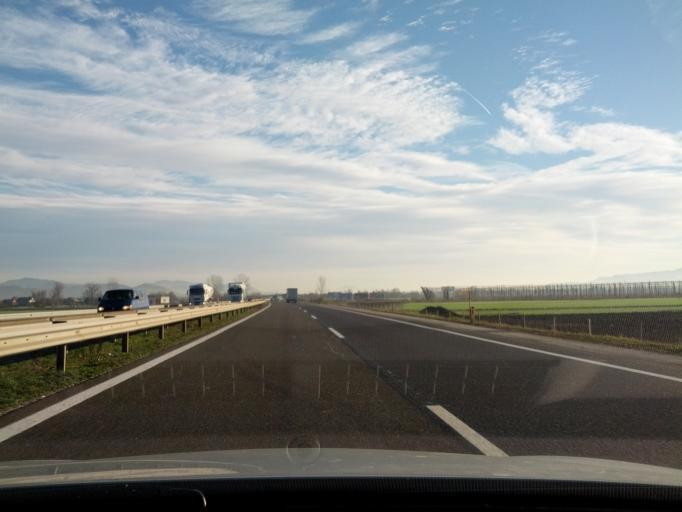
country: SI
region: Braslovce
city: Braslovce
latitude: 46.2572
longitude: 15.0441
